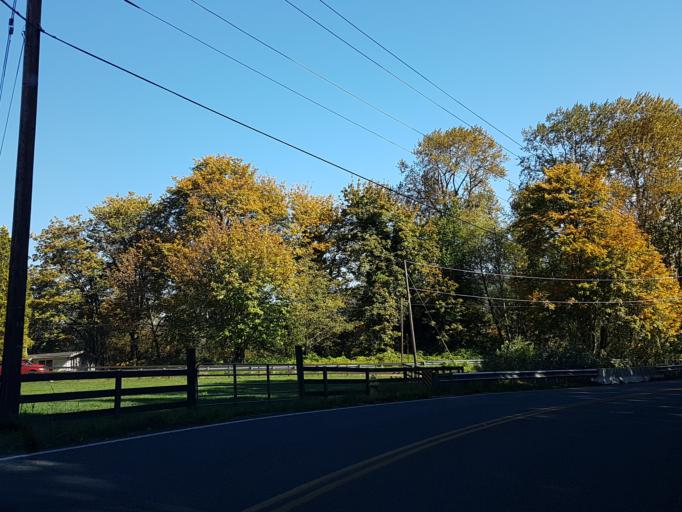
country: US
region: Washington
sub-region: Snohomish County
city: Cathcart
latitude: 47.8432
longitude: -122.0910
